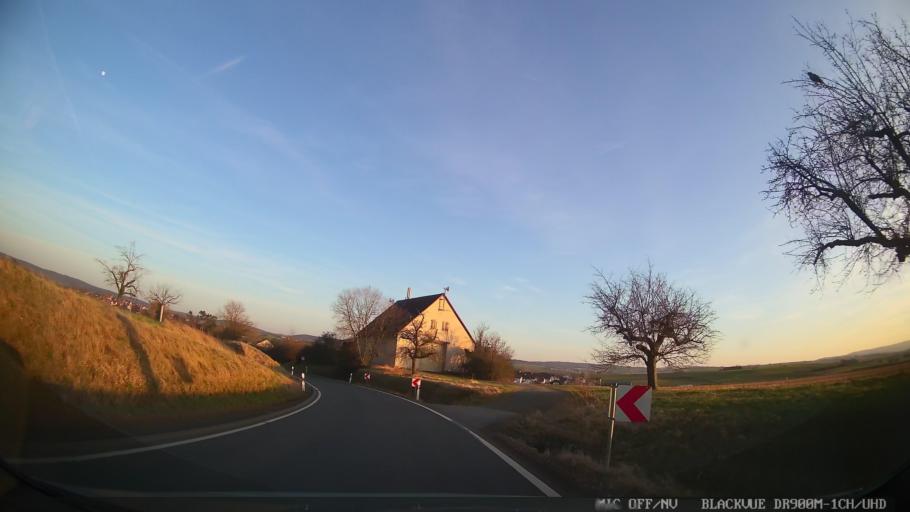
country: DE
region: Hesse
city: Reinheim
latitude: 49.8521
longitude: 8.8710
